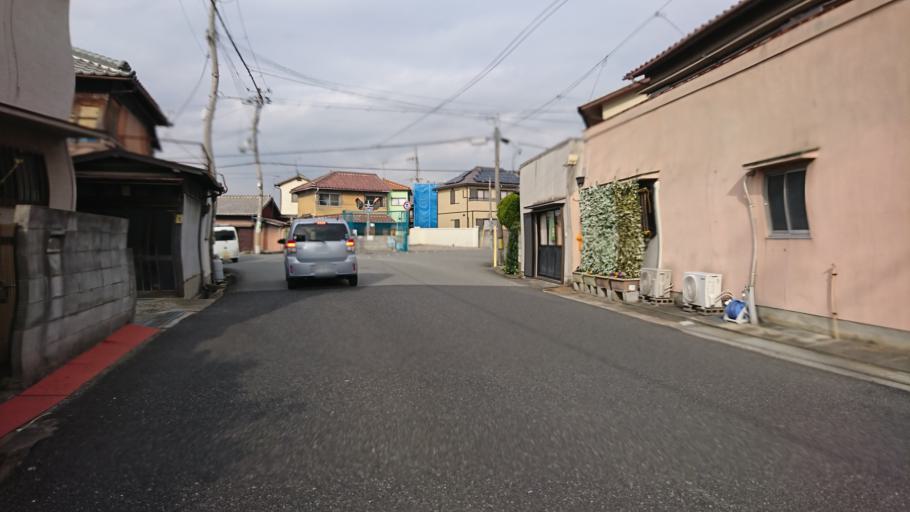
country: JP
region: Hyogo
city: Kakogawacho-honmachi
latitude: 34.7645
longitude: 134.8579
